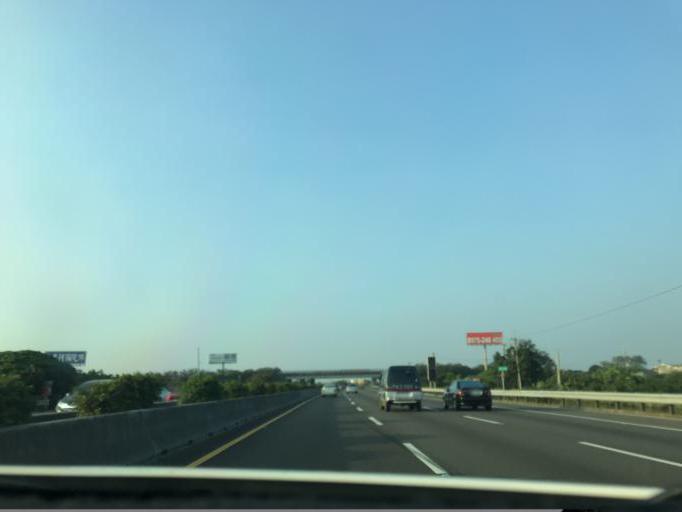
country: TW
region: Taiwan
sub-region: Tainan
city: Tainan
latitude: 23.1429
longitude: 120.2326
